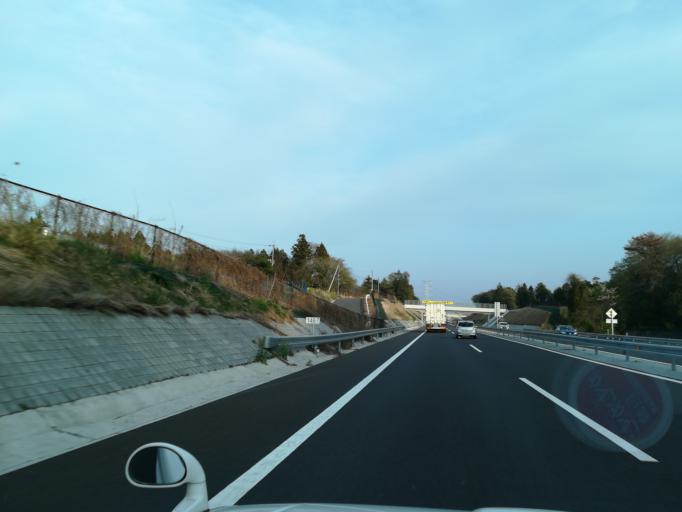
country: JP
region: Ibaraki
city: Mitsukaido
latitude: 36.0657
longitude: 140.0276
